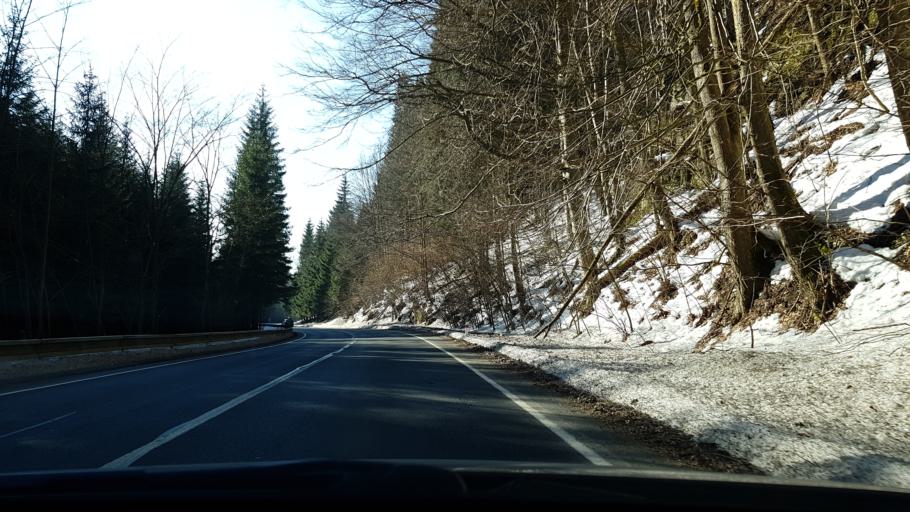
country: CZ
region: Olomoucky
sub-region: Okres Sumperk
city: Stare Mesto
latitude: 50.1407
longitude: 17.0120
